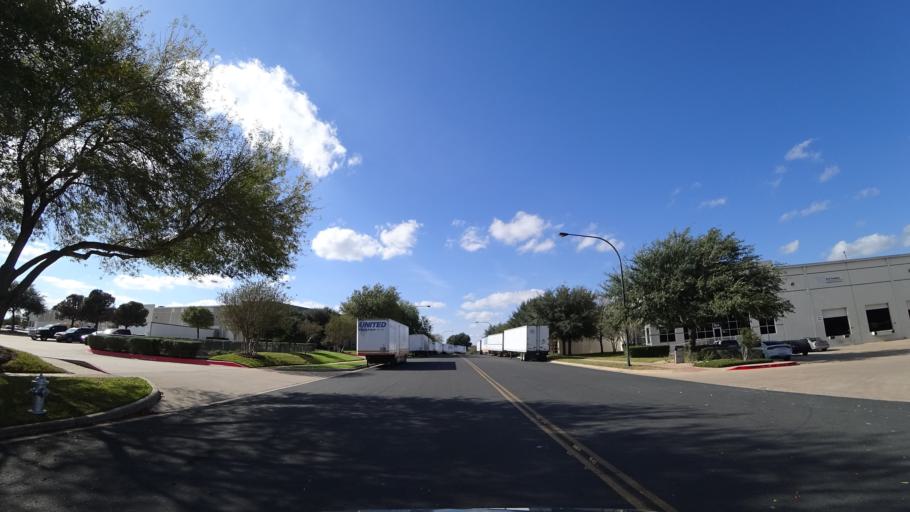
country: US
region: Texas
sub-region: Travis County
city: Wells Branch
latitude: 30.4592
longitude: -97.6744
